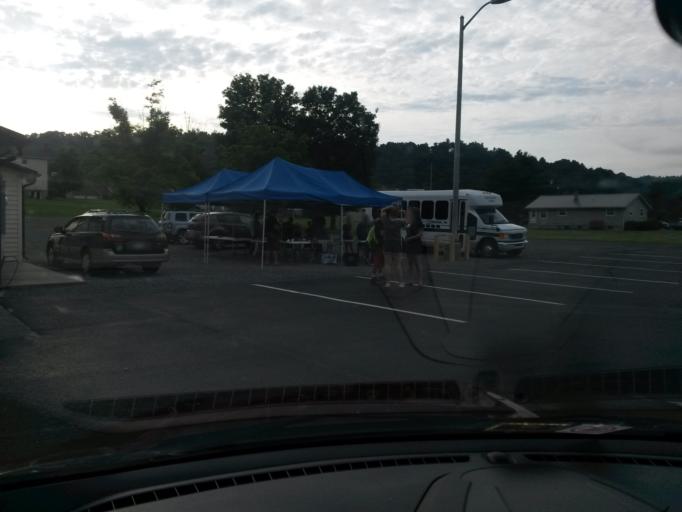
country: US
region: Virginia
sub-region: City of Covington
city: Fairlawn
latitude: 37.7649
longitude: -79.9689
